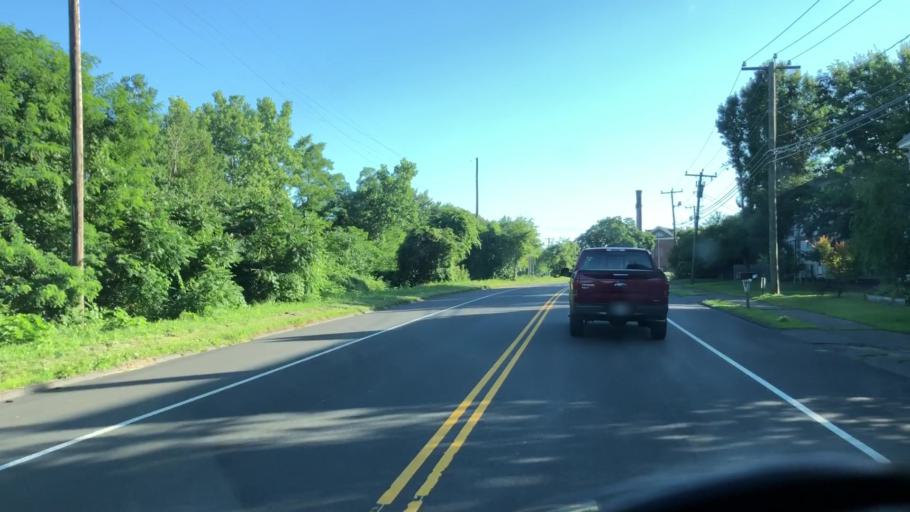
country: US
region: Massachusetts
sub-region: Hampshire County
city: Easthampton
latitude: 42.2772
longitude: -72.6560
